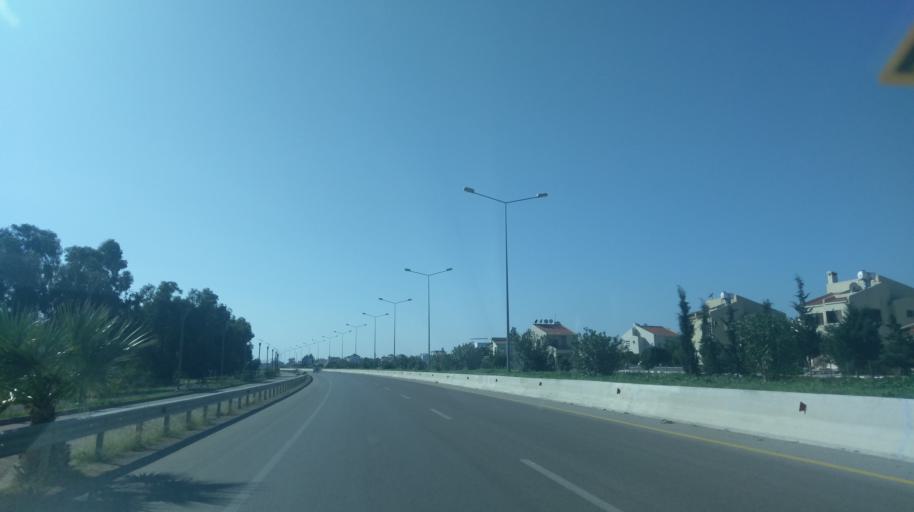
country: CY
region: Ammochostos
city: Trikomo
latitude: 35.2748
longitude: 33.9176
